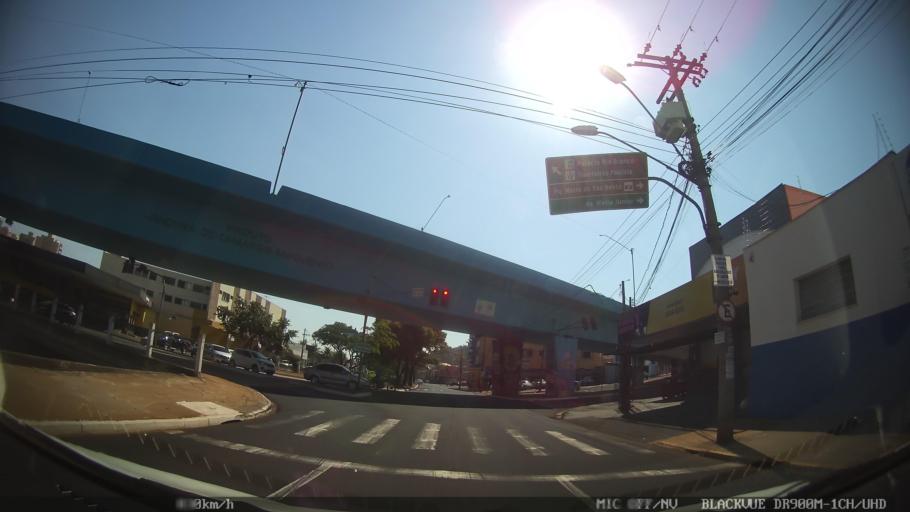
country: BR
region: Sao Paulo
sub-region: Ribeirao Preto
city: Ribeirao Preto
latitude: -21.1805
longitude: -47.8003
